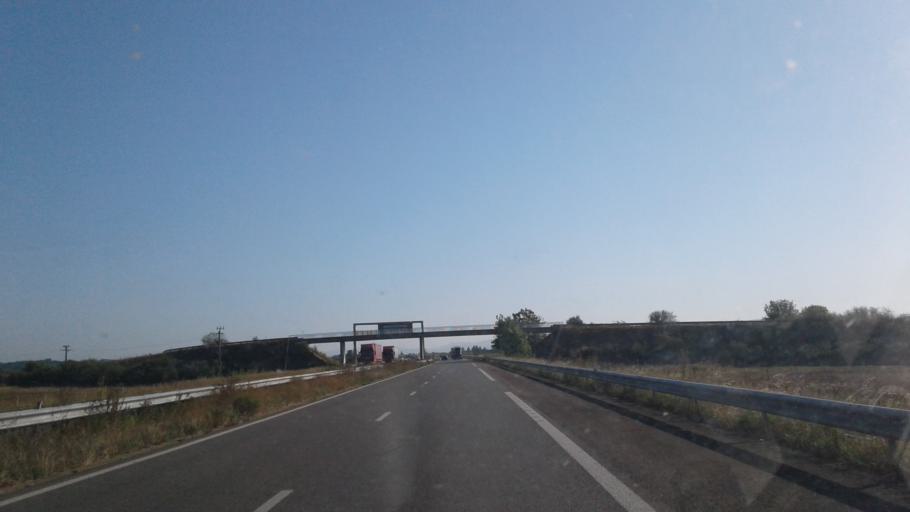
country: FR
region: Rhone-Alpes
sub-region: Departement de l'Ain
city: Meximieux
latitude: 45.8723
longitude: 5.1992
